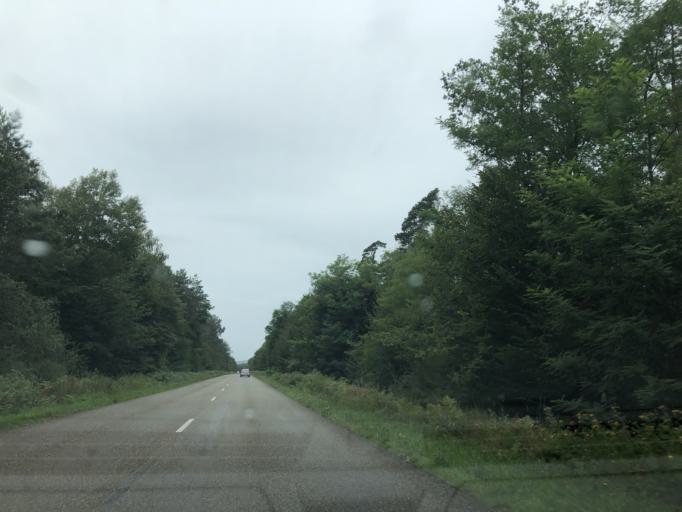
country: DE
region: Rheinland-Pfalz
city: Kapsweyer
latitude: 49.0119
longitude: 8.0360
